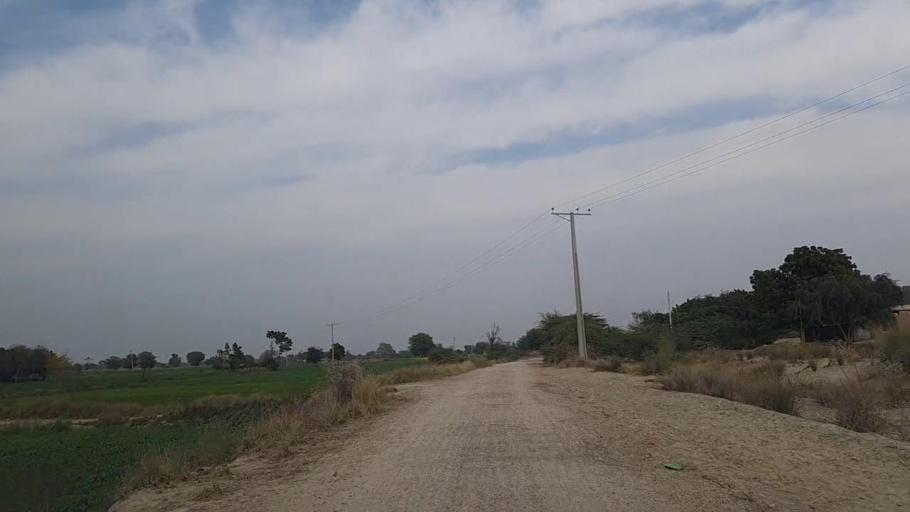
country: PK
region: Sindh
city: Daur
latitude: 26.4351
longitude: 68.4701
